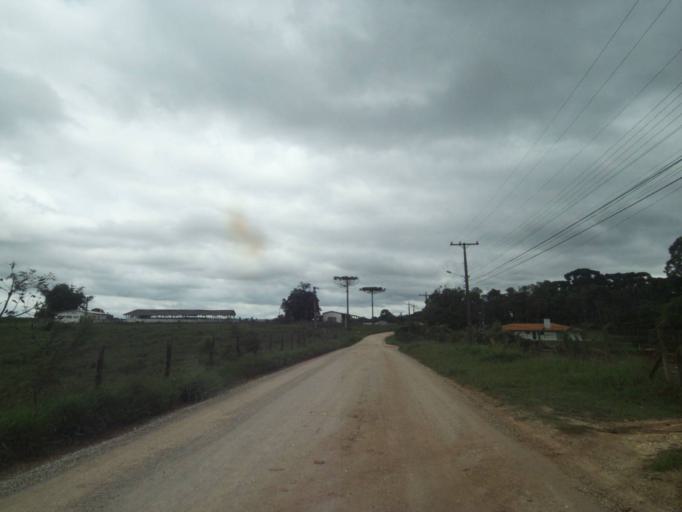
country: BR
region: Parana
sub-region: Campina Grande Do Sul
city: Campina Grande do Sul
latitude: -25.3251
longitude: -49.0881
